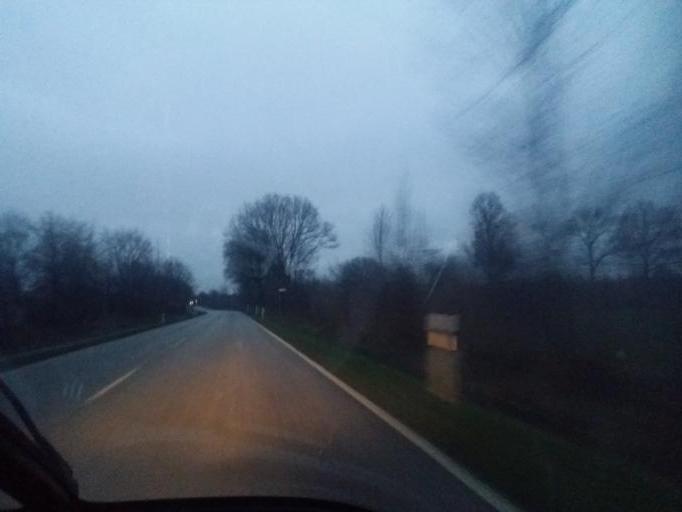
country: DE
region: Schleswig-Holstein
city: Schenefeld
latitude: 54.0592
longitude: 9.4761
